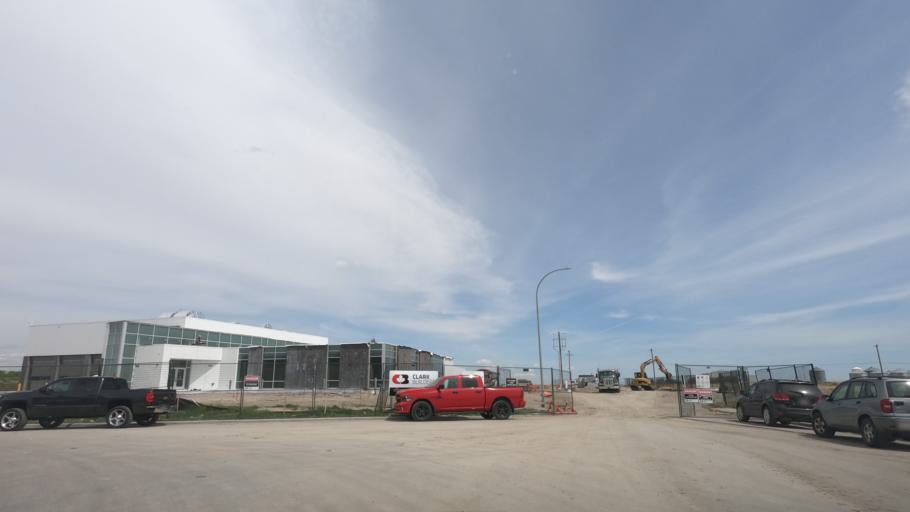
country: CA
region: Alberta
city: Airdrie
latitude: 51.3027
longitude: -113.9810
